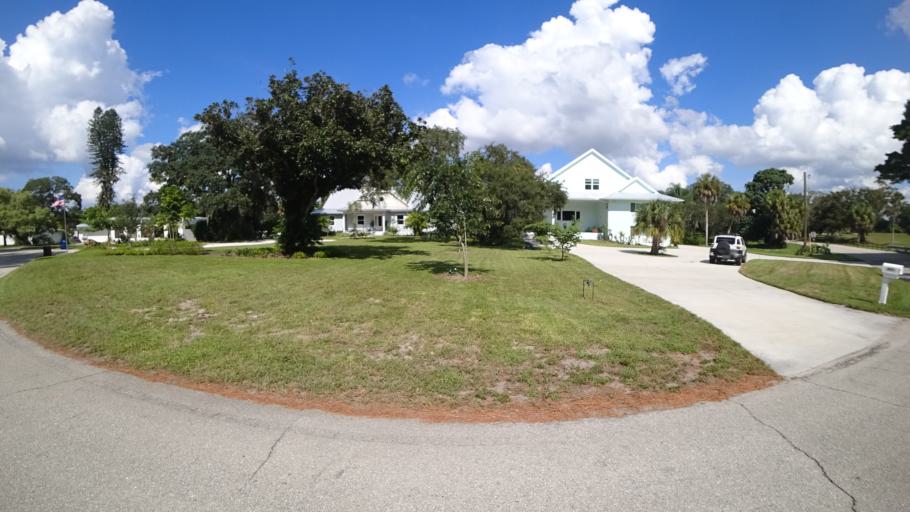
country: US
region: Florida
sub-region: Manatee County
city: Whitfield
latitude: 27.4171
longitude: -82.5663
